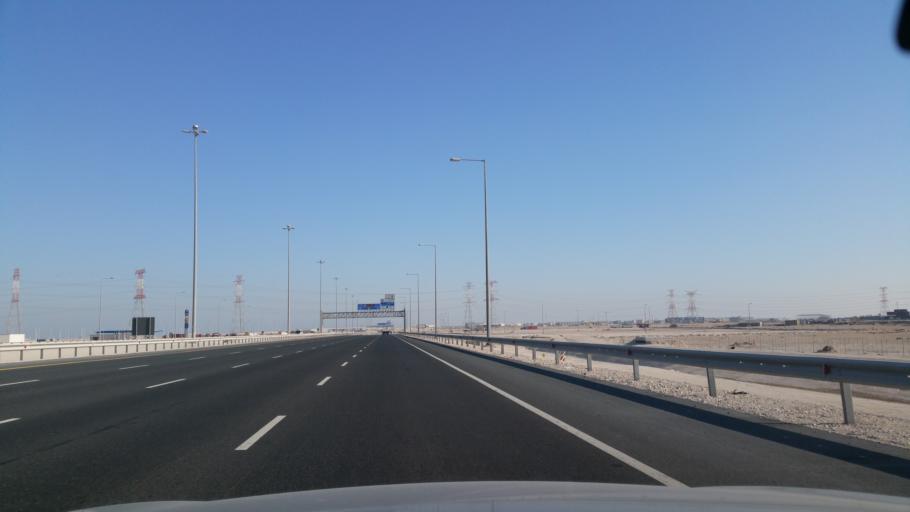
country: QA
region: Al Wakrah
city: Al Wukayr
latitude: 25.1073
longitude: 51.5024
